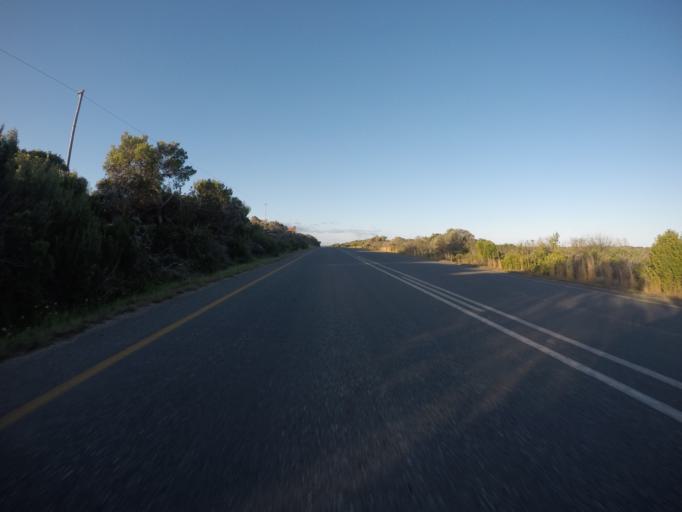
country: ZA
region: Western Cape
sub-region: Eden District Municipality
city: Riversdale
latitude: -34.3879
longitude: 21.4005
